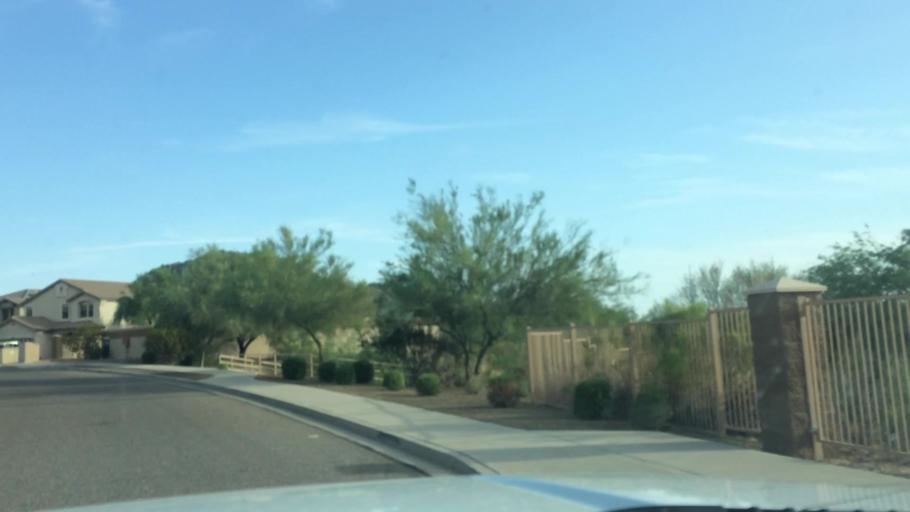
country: US
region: Arizona
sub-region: Maricopa County
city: Cave Creek
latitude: 33.6942
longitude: -112.0454
